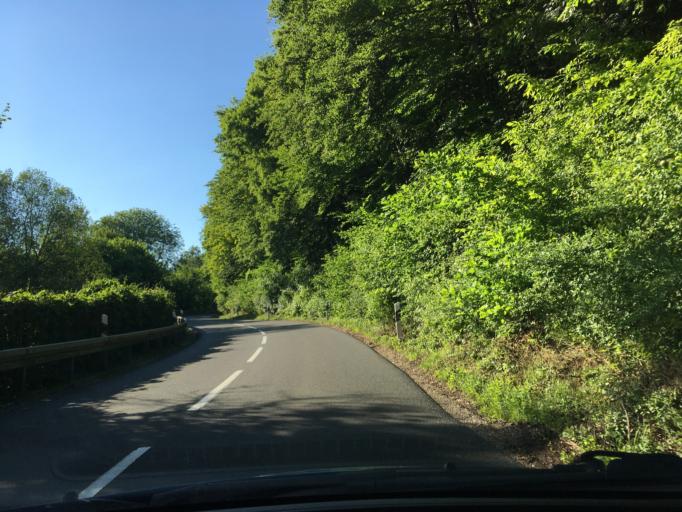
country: DE
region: Lower Saxony
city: Coppengrave
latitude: 51.9810
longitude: 9.7445
